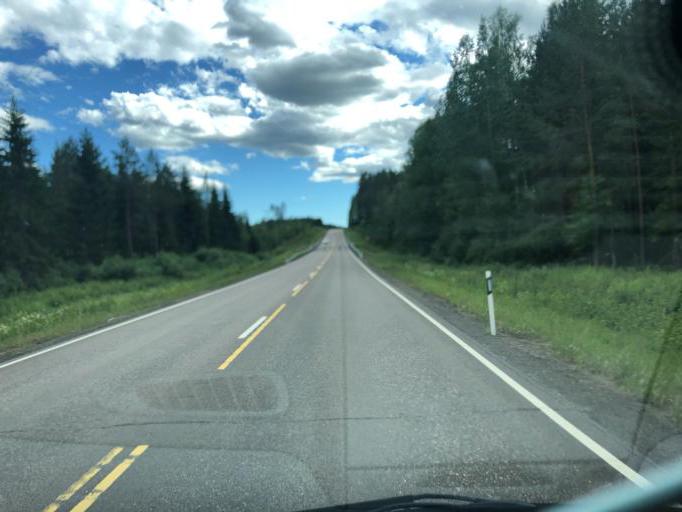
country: FI
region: Southern Savonia
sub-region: Mikkeli
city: Maentyharju
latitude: 61.0789
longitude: 27.0616
